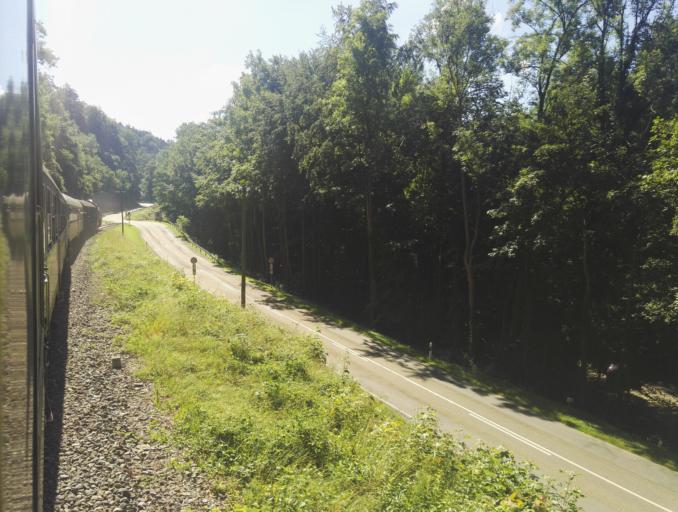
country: DE
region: Baden-Wuerttemberg
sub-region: Regierungsbezirk Stuttgart
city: Althutte
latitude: 48.8936
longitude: 9.5902
